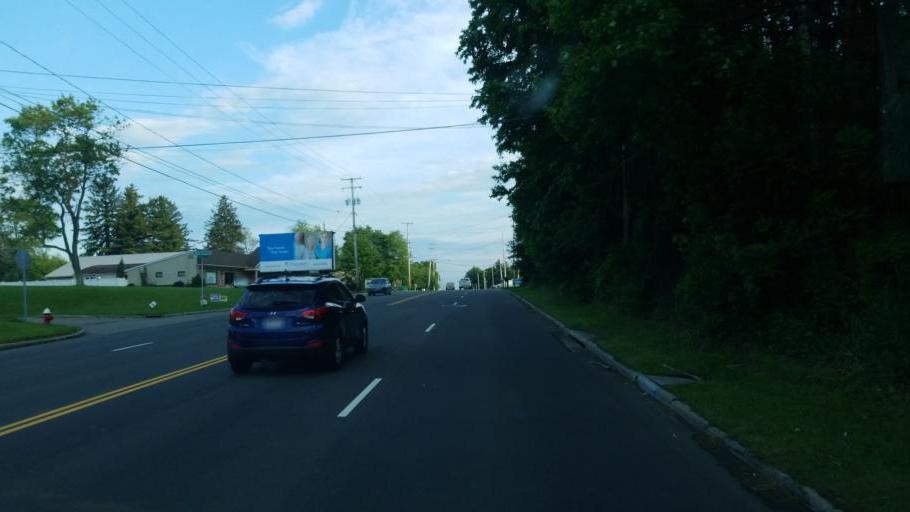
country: US
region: Ohio
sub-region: Stark County
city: Uniontown
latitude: 40.9521
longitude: -81.4068
